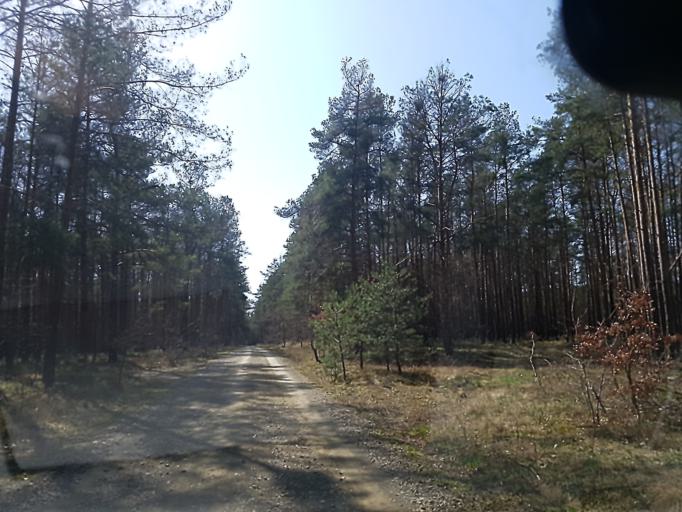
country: DE
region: Brandenburg
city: Schonborn
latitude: 51.5892
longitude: 13.4880
